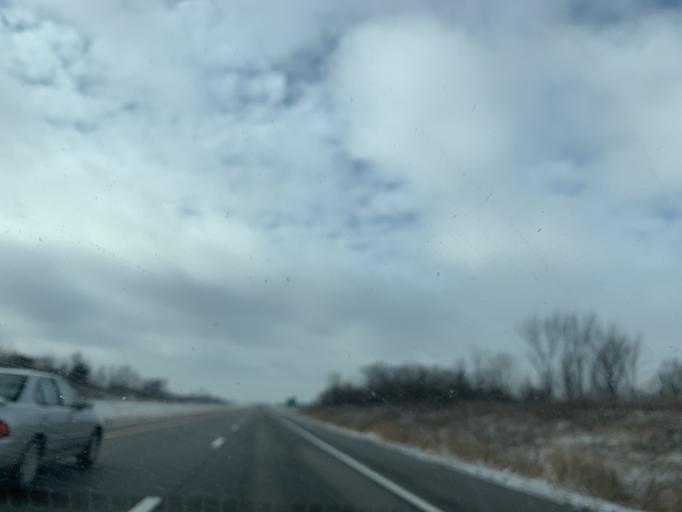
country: US
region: Ohio
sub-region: Licking County
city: Johnstown
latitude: 40.0807
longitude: -82.7118
